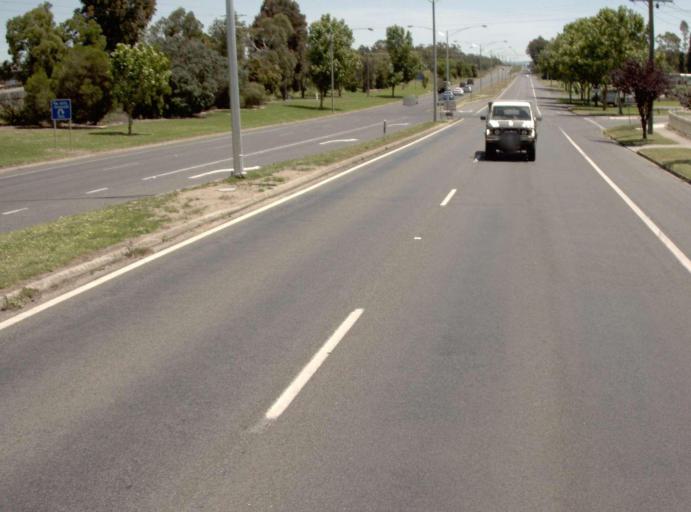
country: AU
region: Victoria
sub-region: Latrobe
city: Traralgon
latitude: -38.2040
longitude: 146.5155
